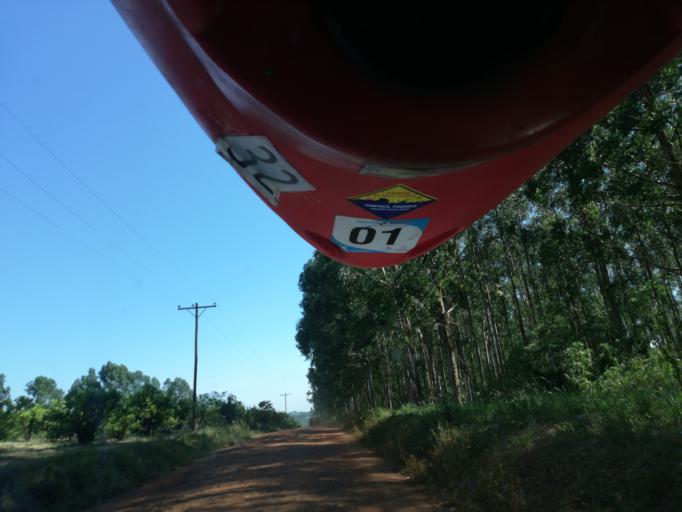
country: AR
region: Misiones
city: Puerto Leoni
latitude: -26.9668
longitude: -55.1527
